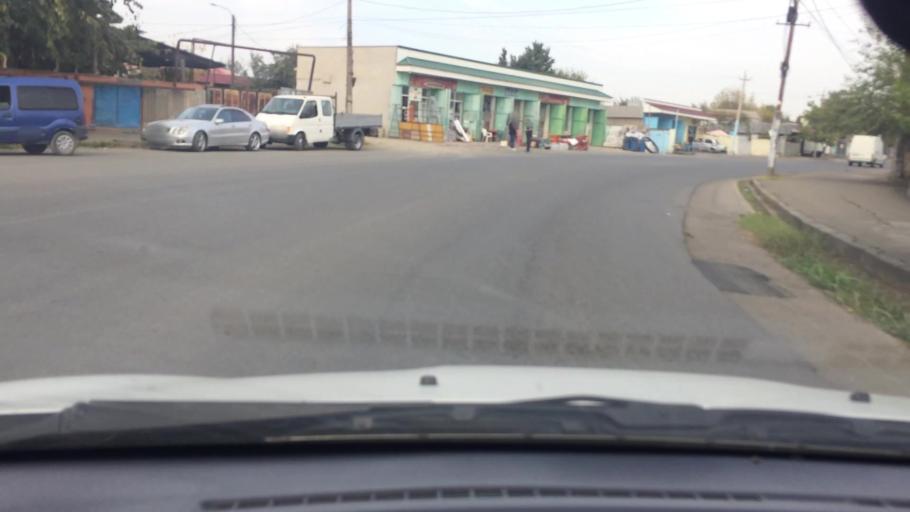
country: GE
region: Kvemo Kartli
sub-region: Marneuli
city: Marneuli
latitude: 41.4634
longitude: 44.8118
